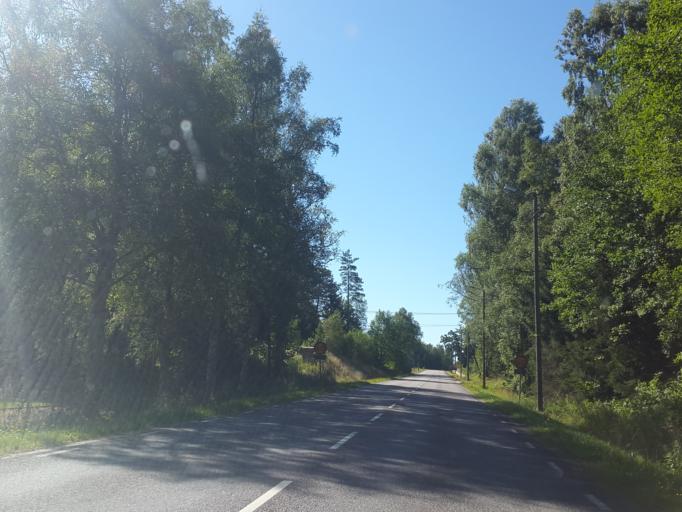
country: SE
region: Vaestra Goetaland
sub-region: Boras Kommun
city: Dalsjofors
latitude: 57.8776
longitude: 13.0315
